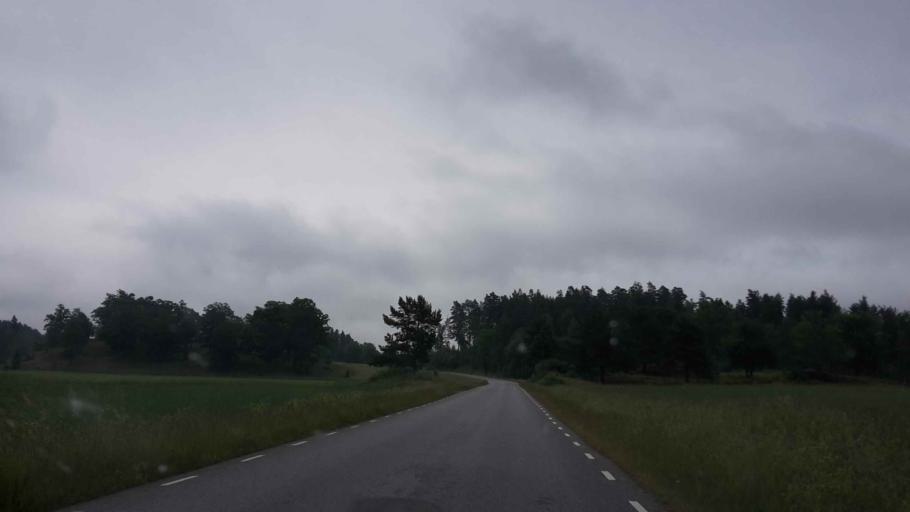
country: SE
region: OEstergoetland
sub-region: Valdemarsviks Kommun
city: Valdemarsvik
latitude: 58.3397
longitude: 16.6149
